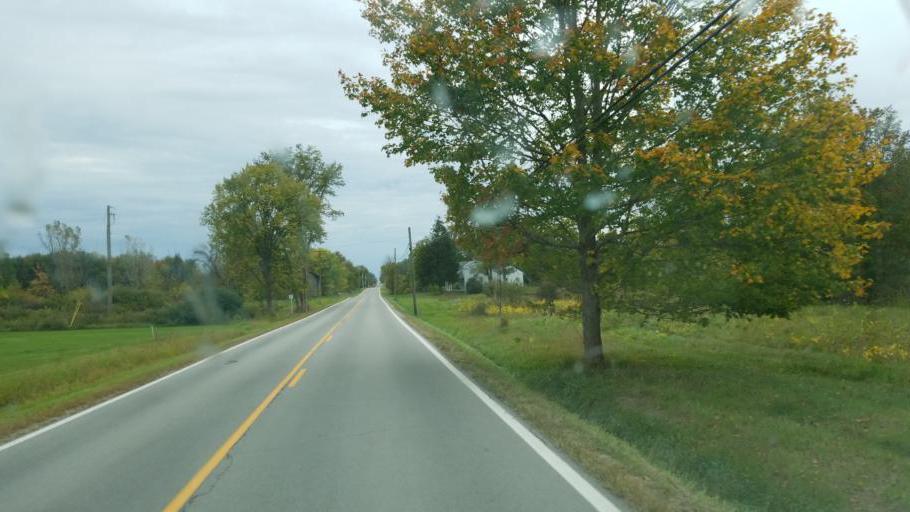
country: US
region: Ohio
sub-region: Huron County
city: Wakeman
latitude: 41.2982
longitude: -82.3729
